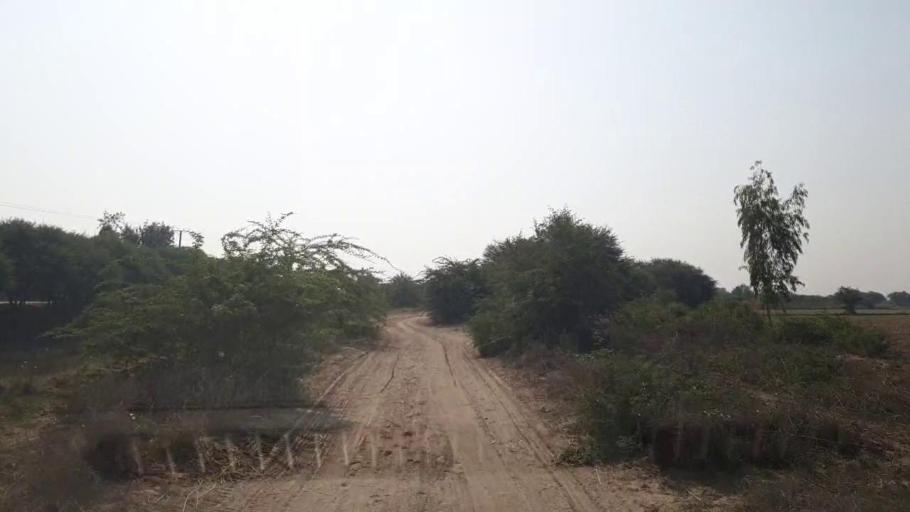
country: PK
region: Sindh
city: Matli
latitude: 24.9532
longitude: 68.6029
